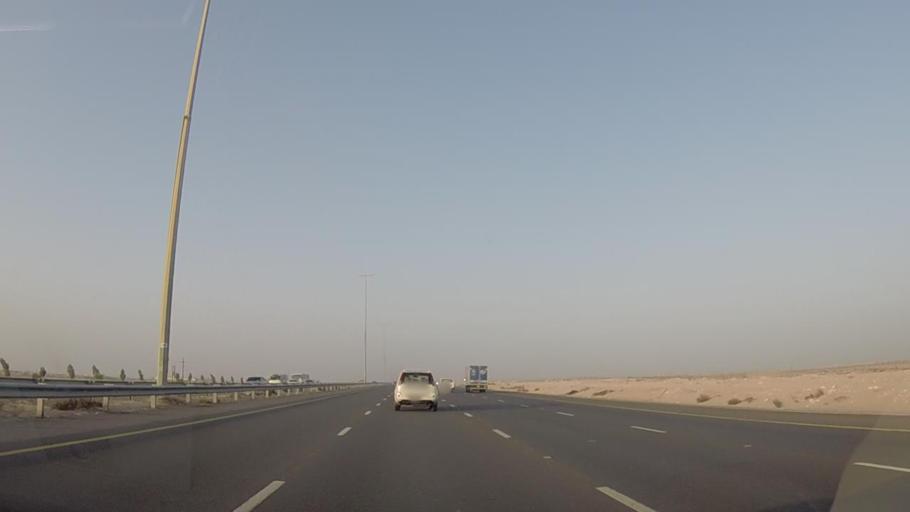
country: AE
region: Dubai
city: Dubai
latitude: 24.9345
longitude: 55.0259
